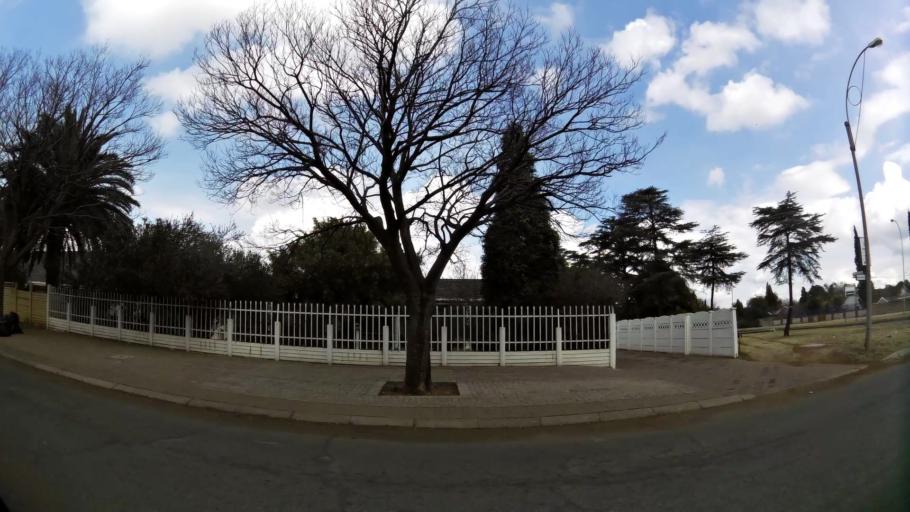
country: ZA
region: Gauteng
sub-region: Sedibeng District Municipality
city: Vanderbijlpark
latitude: -26.7122
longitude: 27.8366
